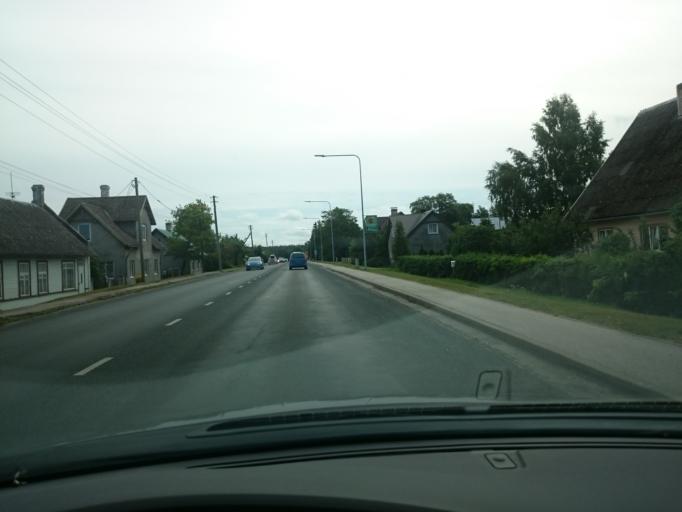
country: EE
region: Laeaene
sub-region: Haapsalu linn
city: Haapsalu
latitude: 58.9375
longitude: 23.5588
